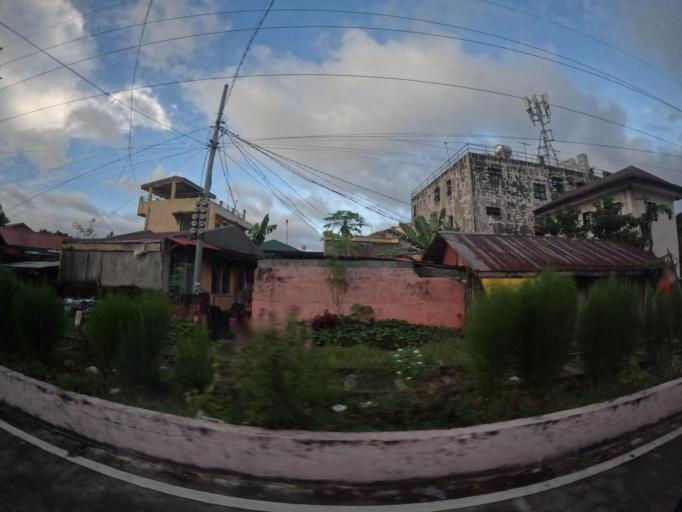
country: PH
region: Bicol
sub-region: Province of Albay
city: Sagpon
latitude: 13.1588
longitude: 123.7397
